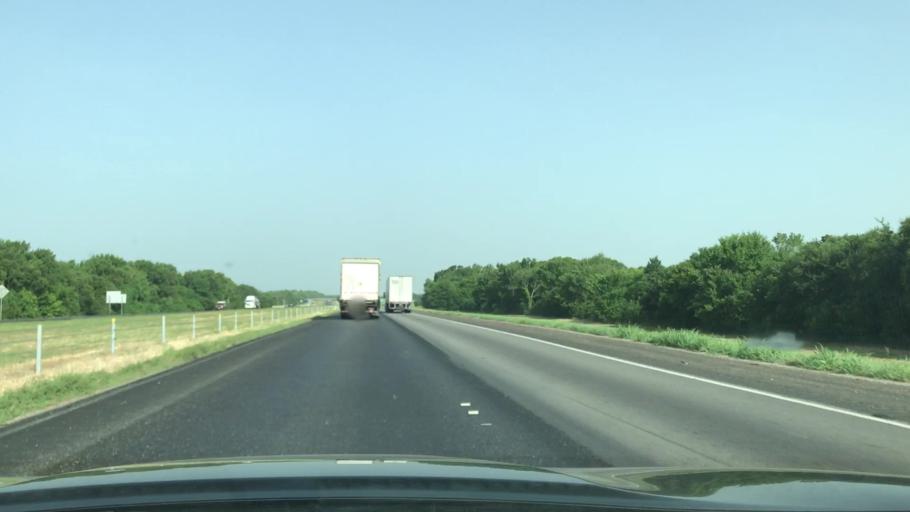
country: US
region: Texas
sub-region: Kaufman County
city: Terrell
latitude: 32.6737
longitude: -96.1654
